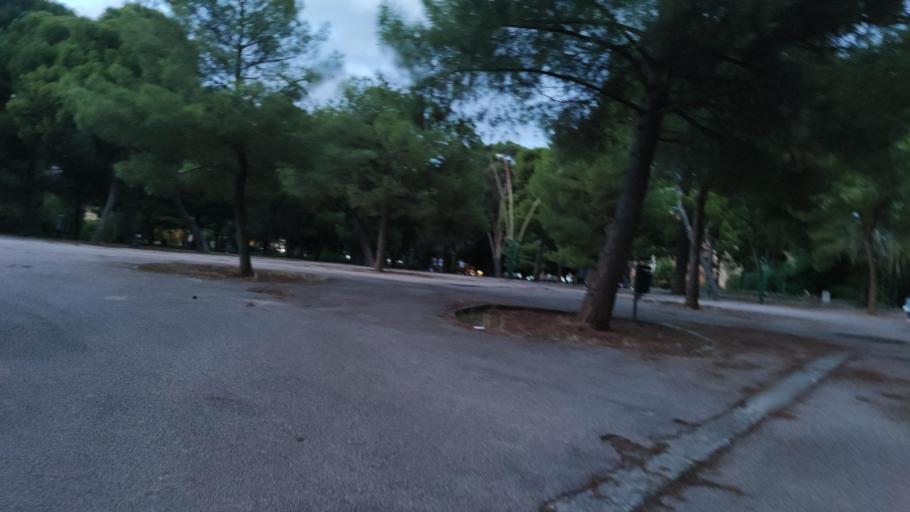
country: IT
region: Sicily
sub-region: Palermo
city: Palermo
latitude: 38.1325
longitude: 13.3516
